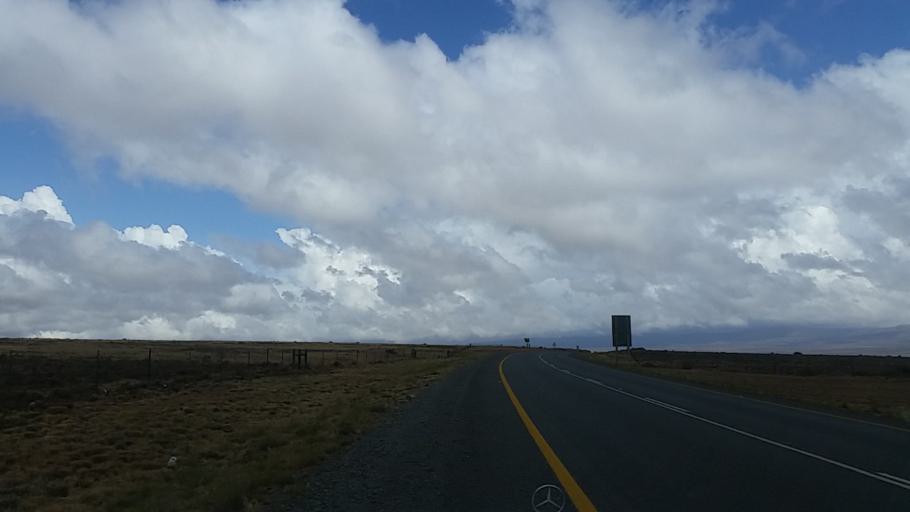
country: ZA
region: Eastern Cape
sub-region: Chris Hani District Municipality
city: Middelburg
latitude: -31.8541
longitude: 24.8726
